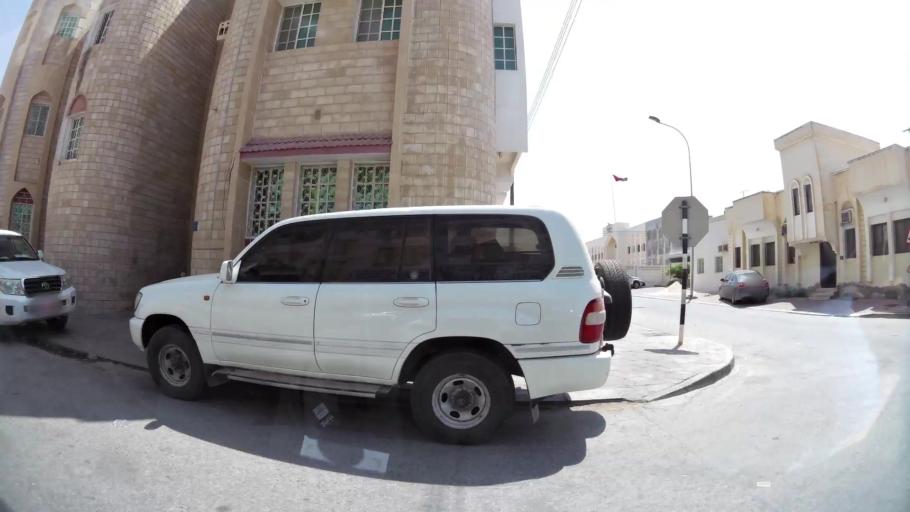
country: OM
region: Zufar
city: Salalah
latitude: 17.0087
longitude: 54.0699
